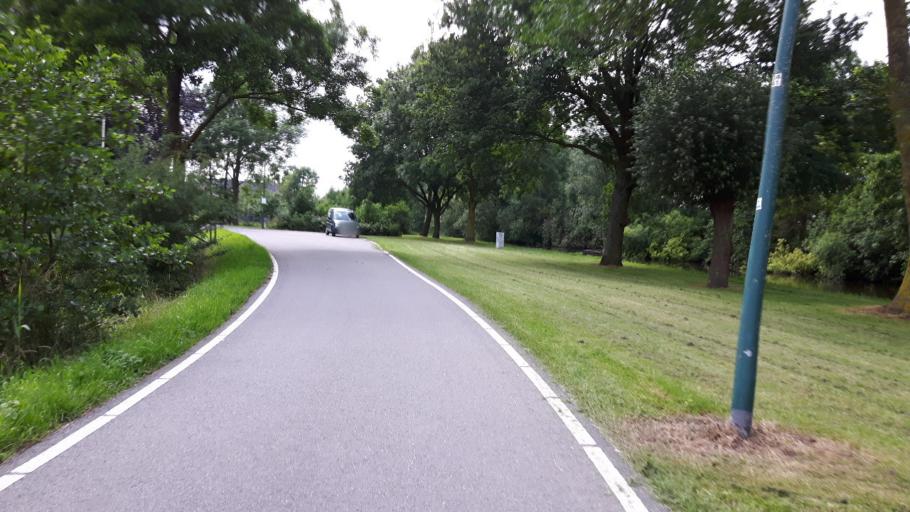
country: NL
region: Utrecht
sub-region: Gemeente Woerden
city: Woerden
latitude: 52.1049
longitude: 4.9312
